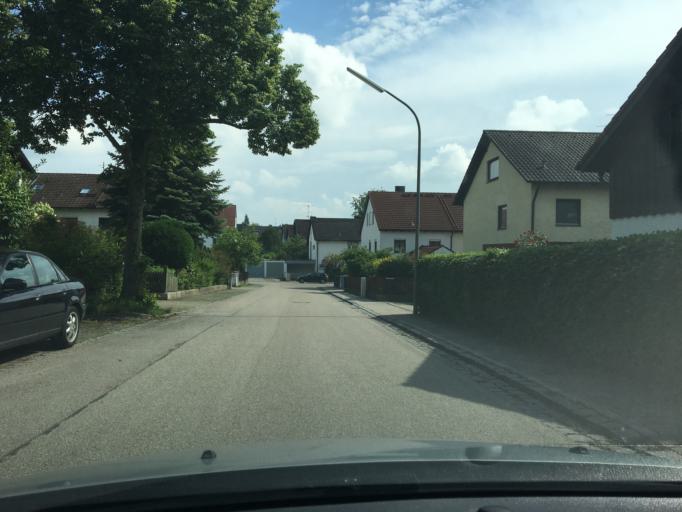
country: DE
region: Bavaria
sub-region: Upper Bavaria
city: Haimhausen
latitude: 48.3152
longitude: 11.5587
